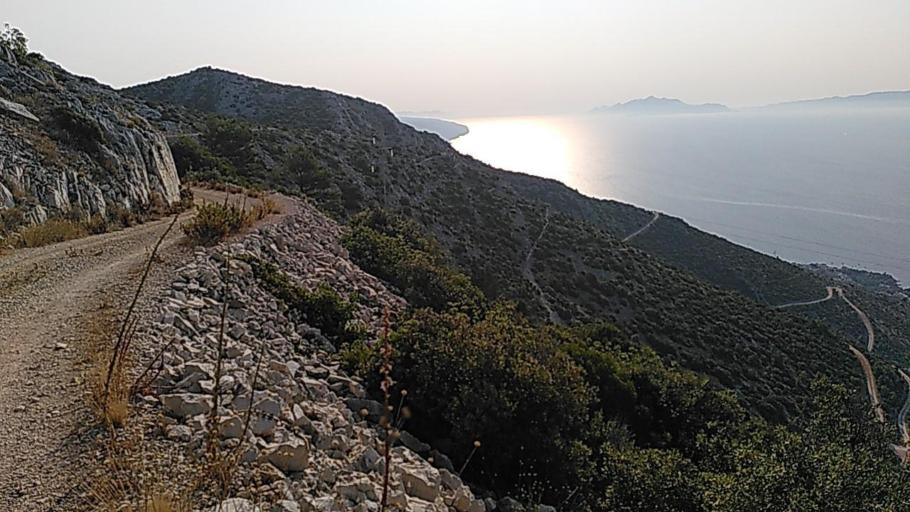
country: HR
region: Splitsko-Dalmatinska
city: Jelsa
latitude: 43.1332
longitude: 16.6748
